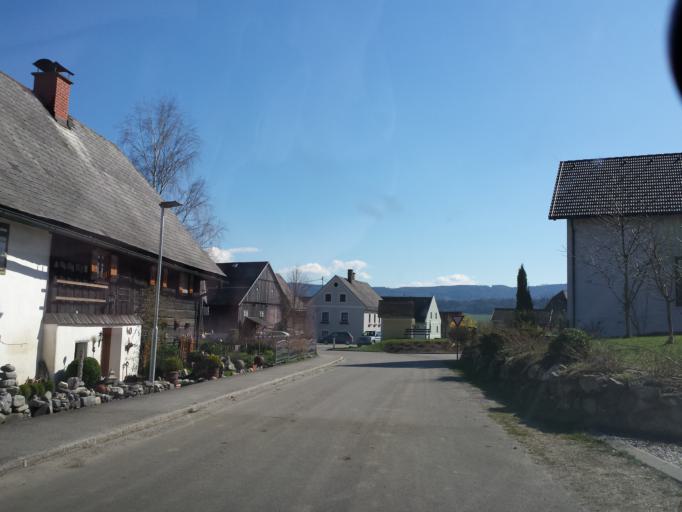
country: AT
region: Styria
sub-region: Politischer Bezirk Leoben
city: Trofaiach
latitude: 47.4202
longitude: 14.9600
